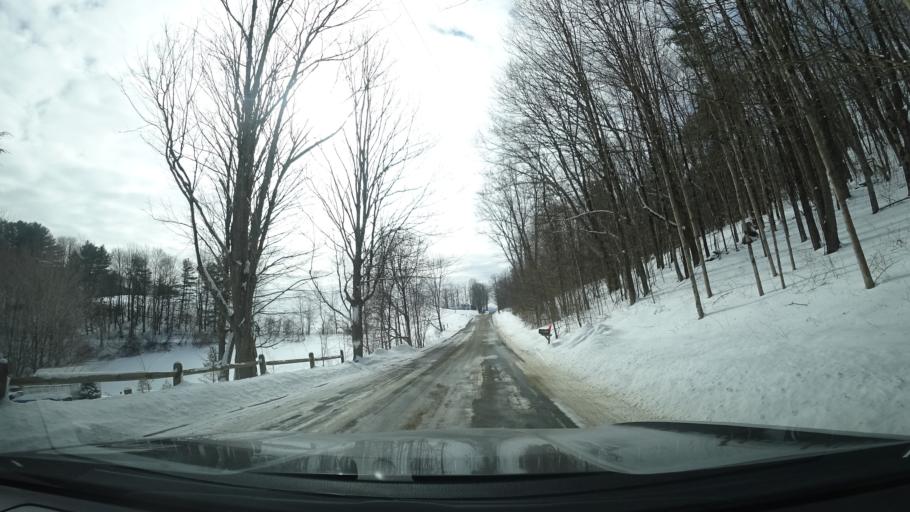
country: US
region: New York
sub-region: Washington County
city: Cambridge
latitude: 43.2123
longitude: -73.3569
